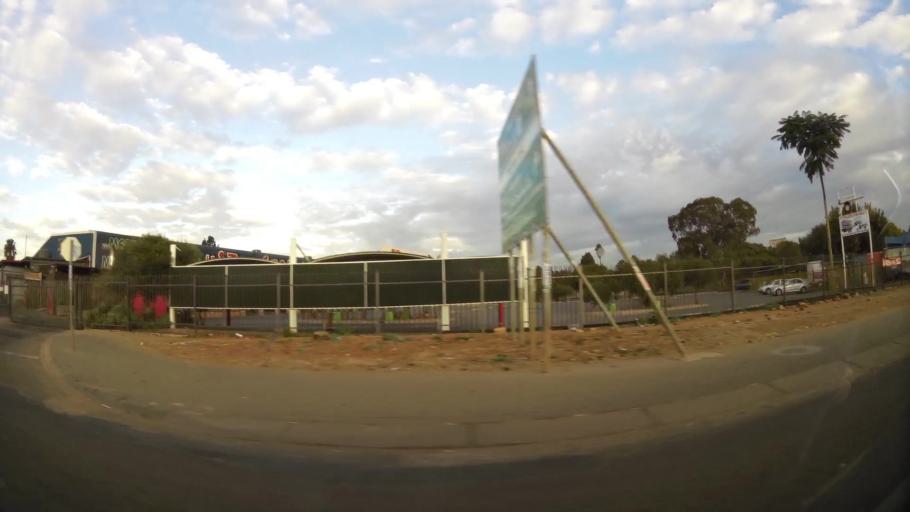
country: ZA
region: Gauteng
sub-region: City of Tshwane Metropolitan Municipality
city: Pretoria
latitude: -25.7337
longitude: 28.3150
